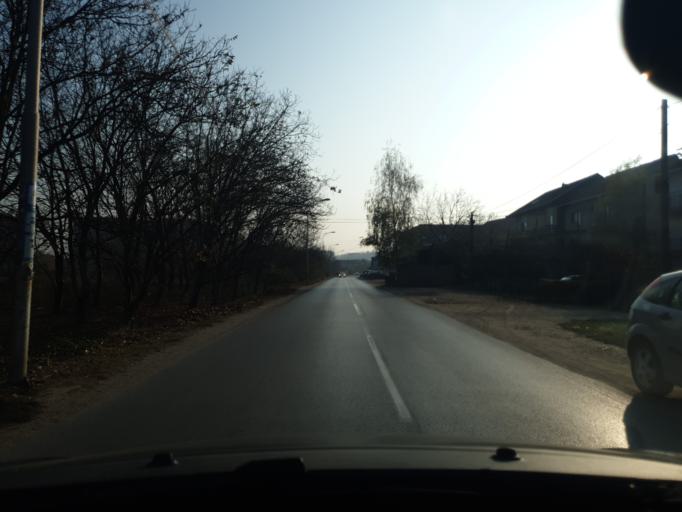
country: RS
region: Central Serbia
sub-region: Jablanicki Okrug
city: Leskovac
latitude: 42.9966
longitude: 21.9251
